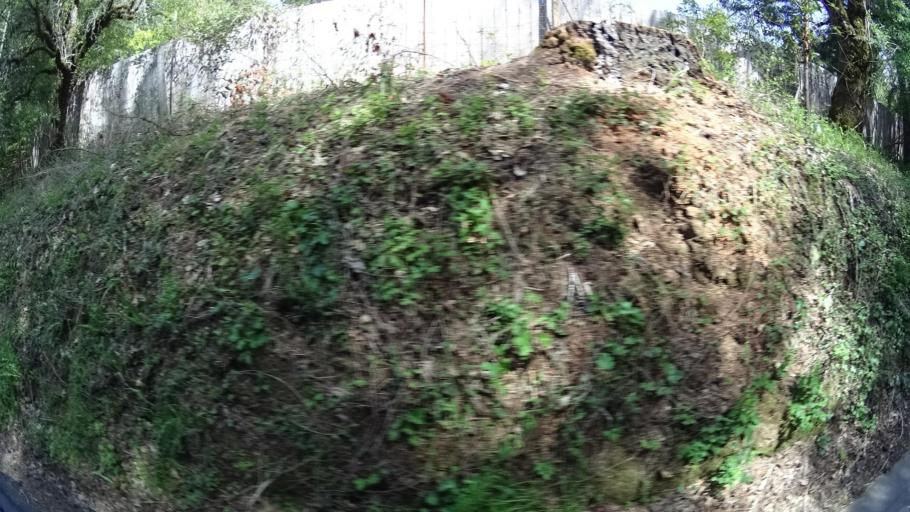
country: US
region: California
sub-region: Humboldt County
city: Redway
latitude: 40.3622
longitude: -123.7288
